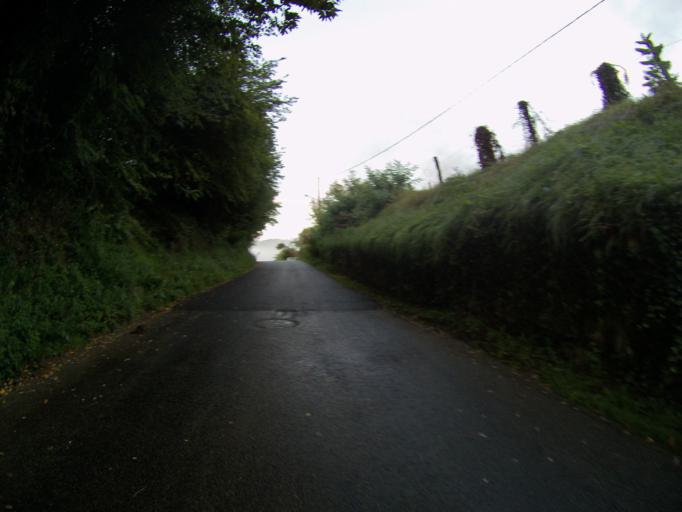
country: FR
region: Aquitaine
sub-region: Departement des Pyrenees-Atlantiques
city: Saint-Jean-Pied-de-Port
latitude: 43.1570
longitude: -1.2461
